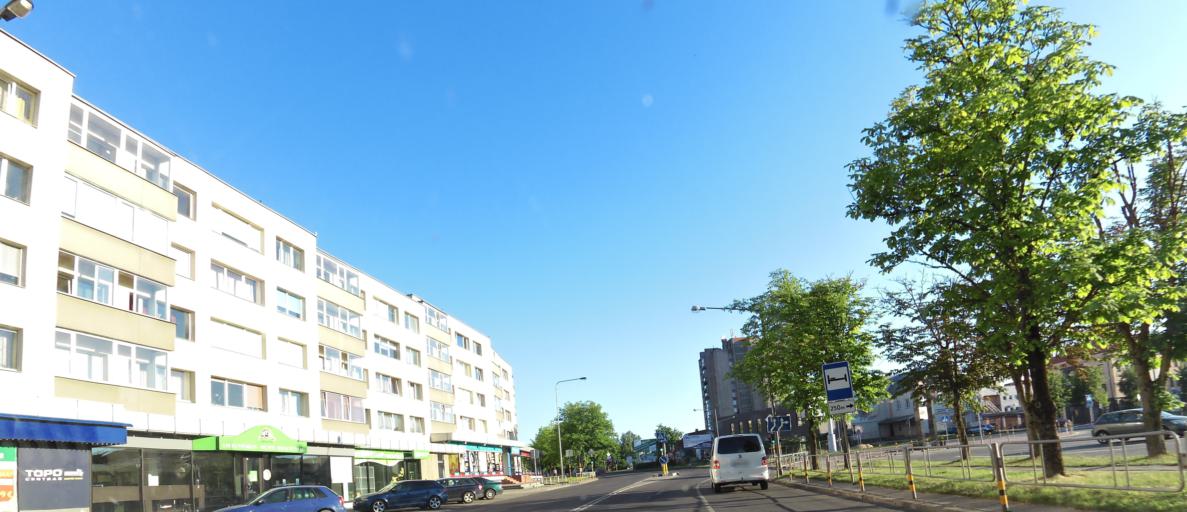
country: LT
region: Panevezys
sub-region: Panevezys City
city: Panevezys
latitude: 55.7273
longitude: 24.3671
